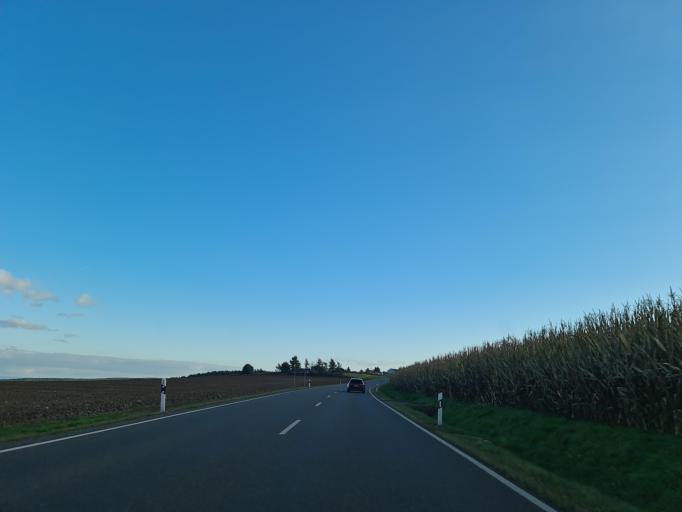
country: DE
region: Thuringia
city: Wildetaube
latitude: 50.7121
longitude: 12.1162
